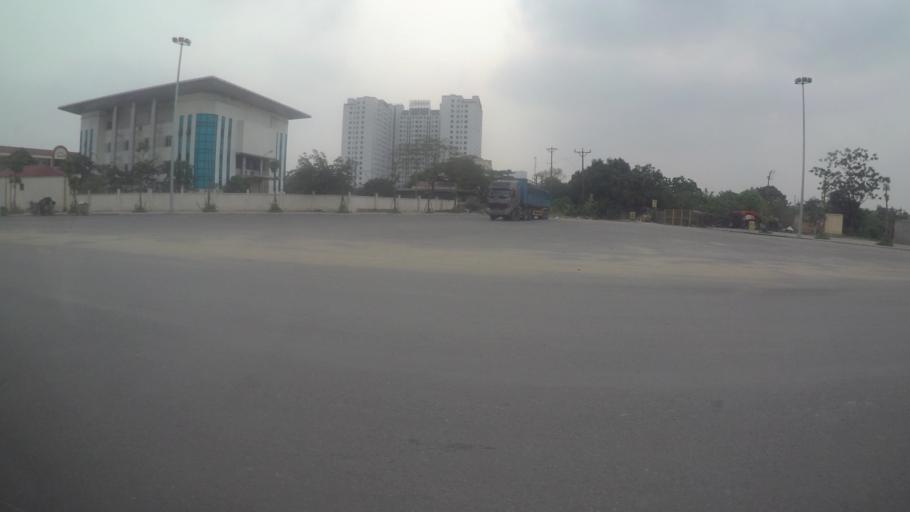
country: VN
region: Ha Noi
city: Cau Dien
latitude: 21.0413
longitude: 105.7379
